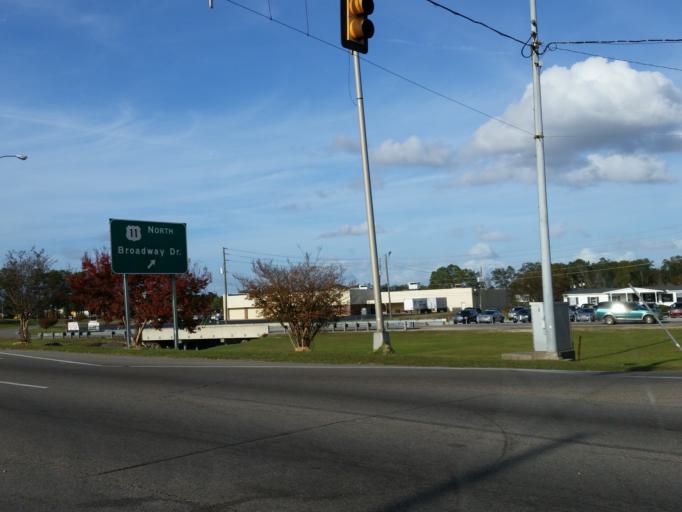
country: US
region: Mississippi
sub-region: Forrest County
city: Hattiesburg
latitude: 31.3050
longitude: -89.3141
